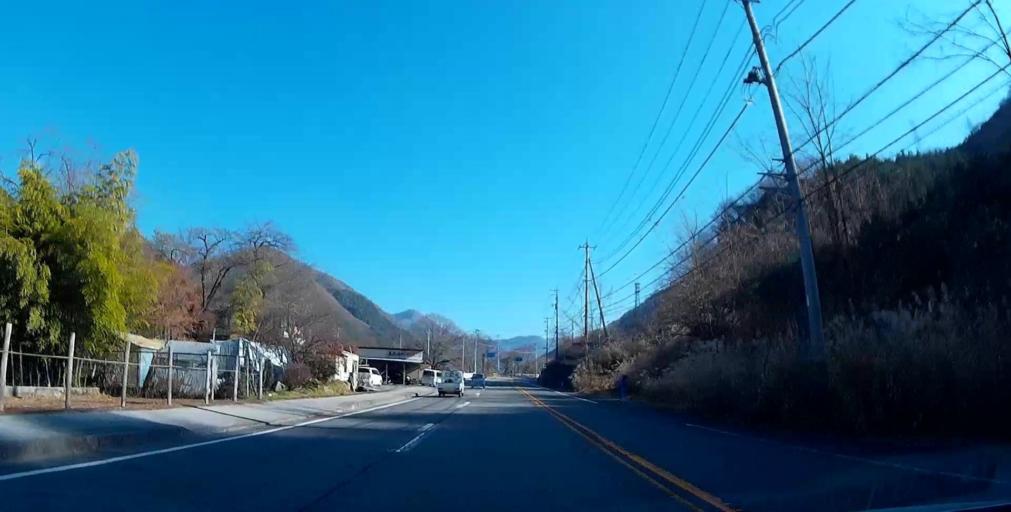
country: JP
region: Yamanashi
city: Isawa
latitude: 35.5921
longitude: 138.7243
